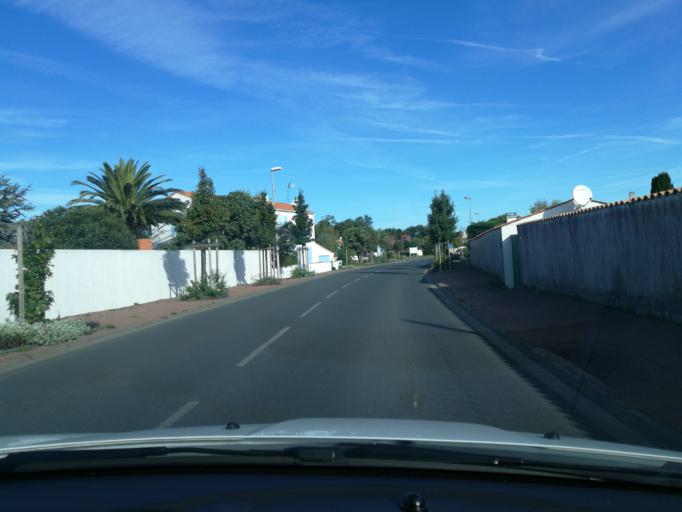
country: FR
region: Poitou-Charentes
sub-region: Departement de la Charente-Maritime
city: Saint-Denis-d'Oleron
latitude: 46.0300
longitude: -1.3800
